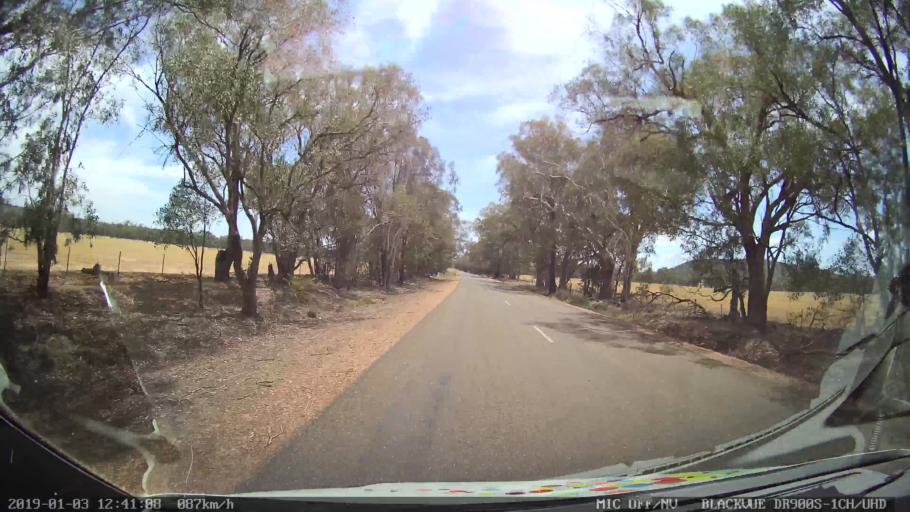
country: AU
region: New South Wales
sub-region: Weddin
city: Grenfell
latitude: -33.8037
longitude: 148.2145
